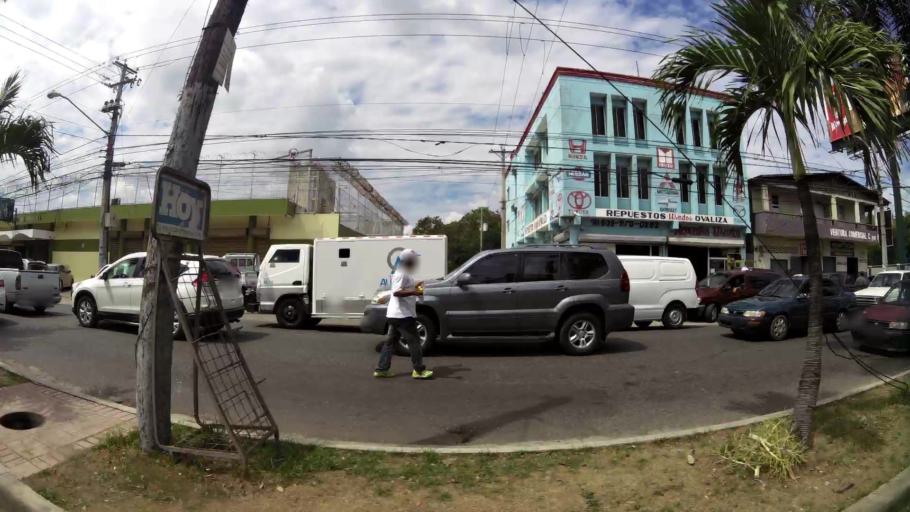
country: DO
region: Santiago
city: Santiago de los Caballeros
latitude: 19.4688
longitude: -70.7126
